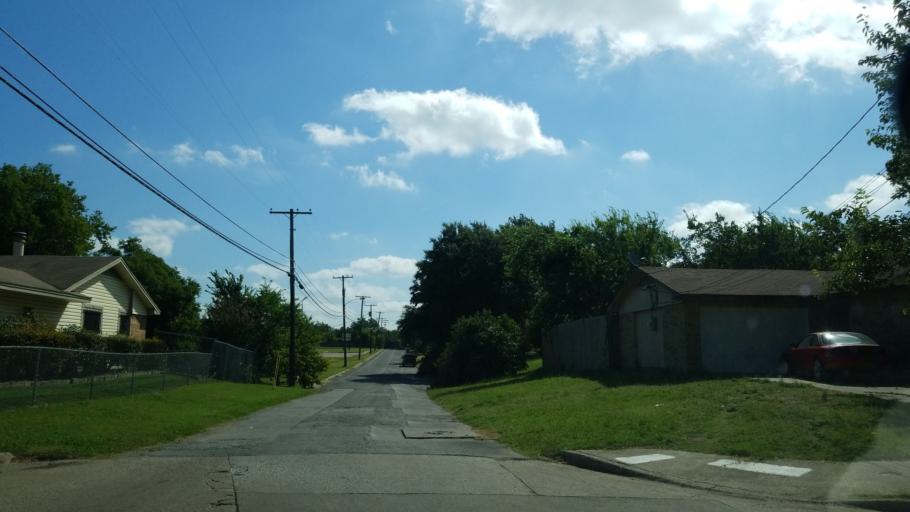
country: US
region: Texas
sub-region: Dallas County
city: Dallas
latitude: 32.7165
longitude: -96.7943
